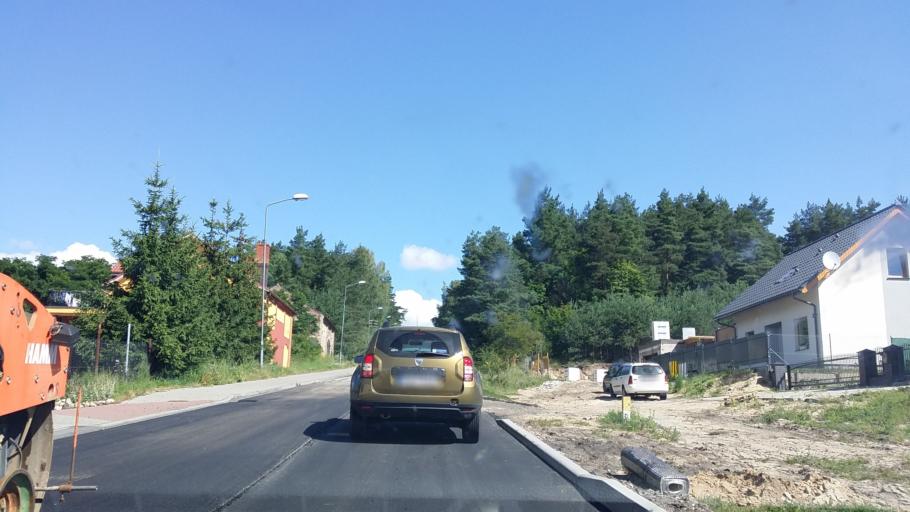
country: PL
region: West Pomeranian Voivodeship
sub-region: Powiat drawski
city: Kalisz Pomorski
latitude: 53.3029
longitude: 15.9092
